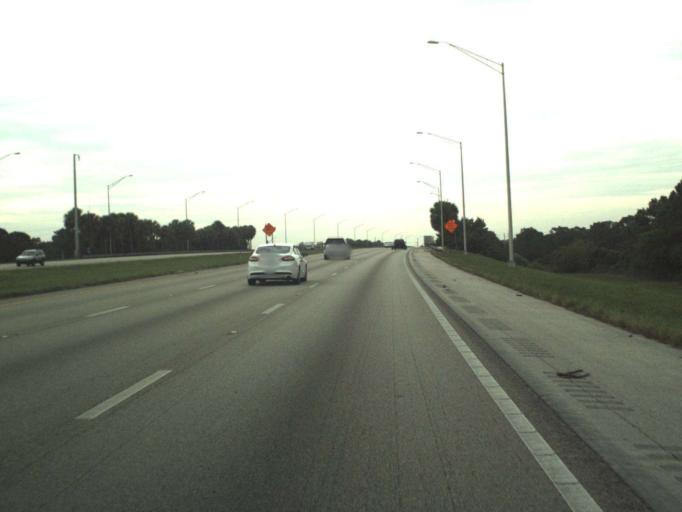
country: US
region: Florida
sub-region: Martin County
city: Palm City
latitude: 27.1260
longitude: -80.2842
